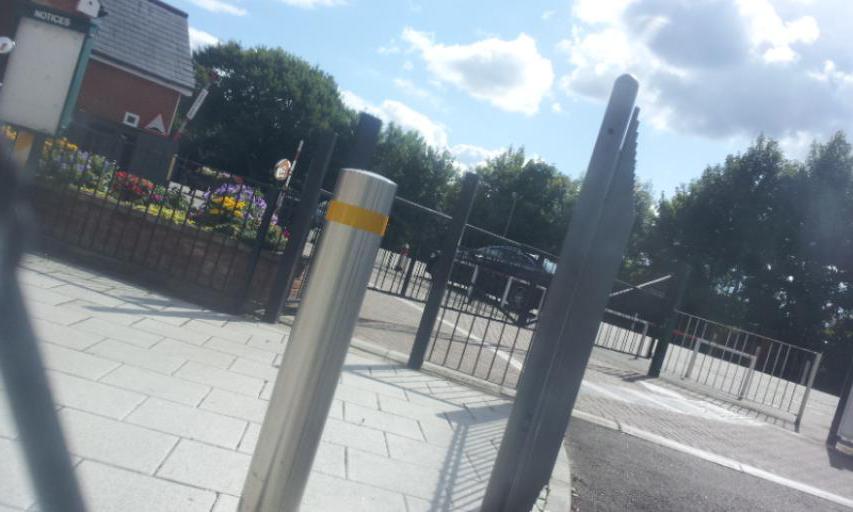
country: GB
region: England
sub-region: Kent
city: Larkfield
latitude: 51.2919
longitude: 0.4185
